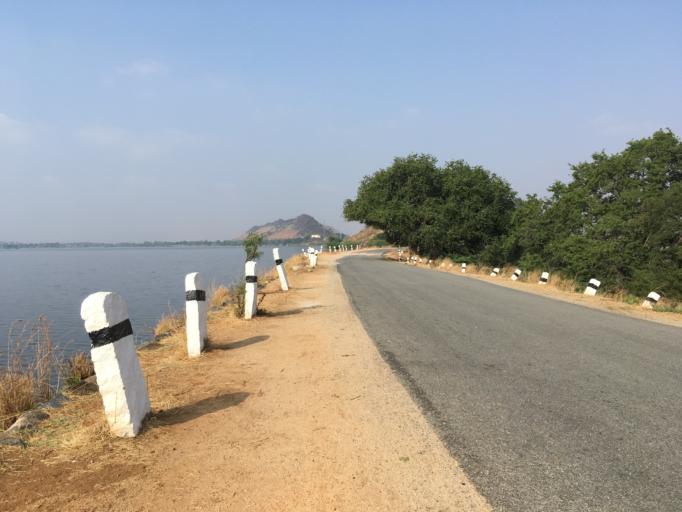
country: IN
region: Andhra Pradesh
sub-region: Anantapur
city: Puttaparthi
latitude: 14.1860
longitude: 77.7830
